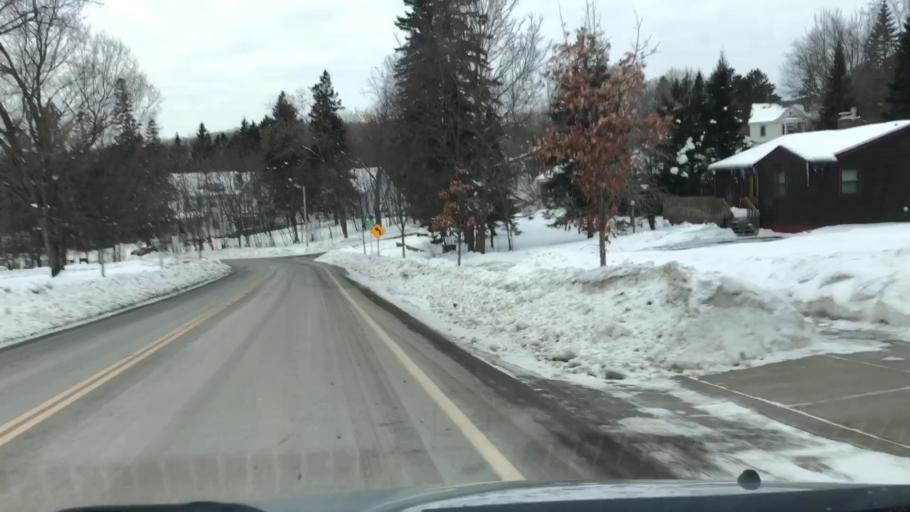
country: US
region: Minnesota
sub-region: Saint Louis County
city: Arnold
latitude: 46.8339
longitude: -92.0701
